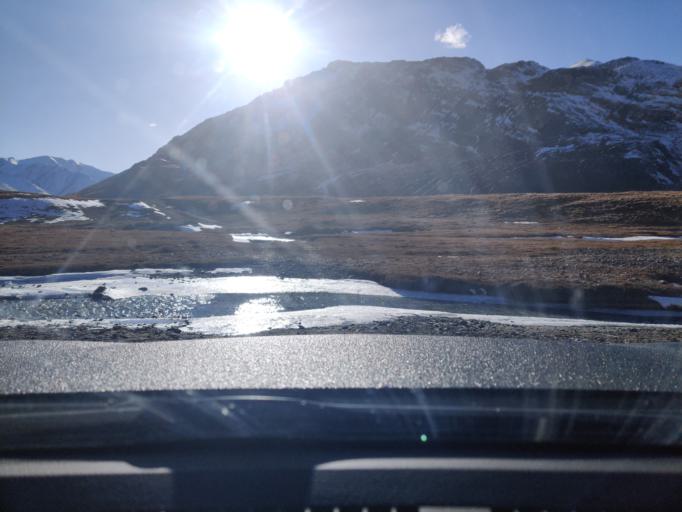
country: KG
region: Ysyk-Koel
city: Kadzhi-Say
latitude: 41.8134
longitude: 77.5805
